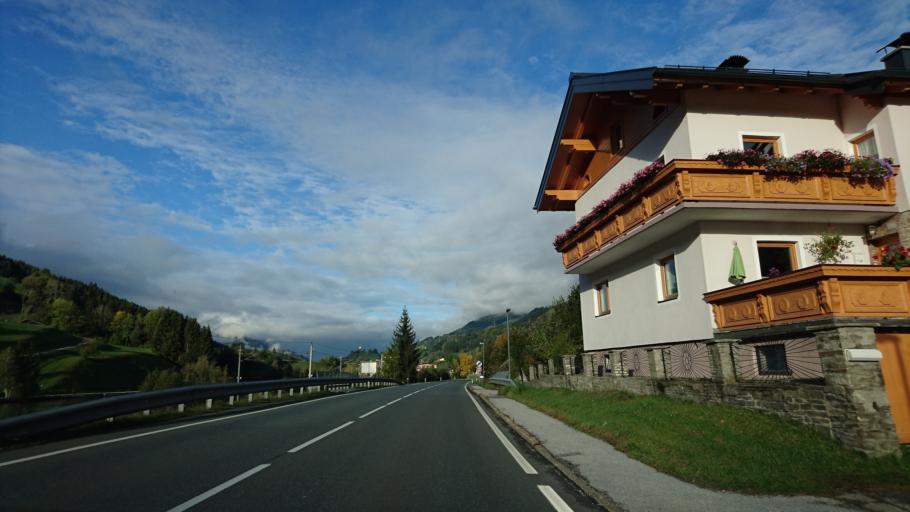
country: AT
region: Salzburg
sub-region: Politischer Bezirk Zell am See
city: Taxenbach
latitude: 47.2888
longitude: 12.9112
